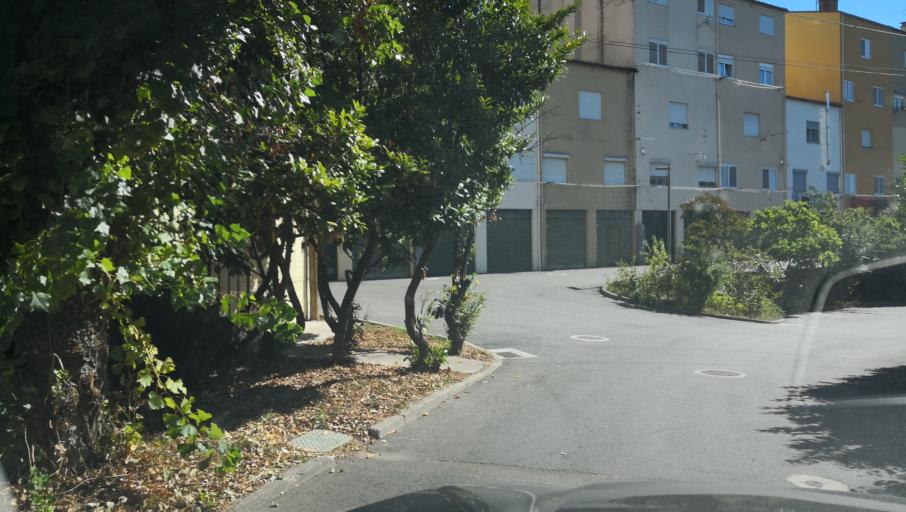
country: PT
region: Vila Real
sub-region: Vila Real
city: Vila Real
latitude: 41.3047
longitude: -7.7484
